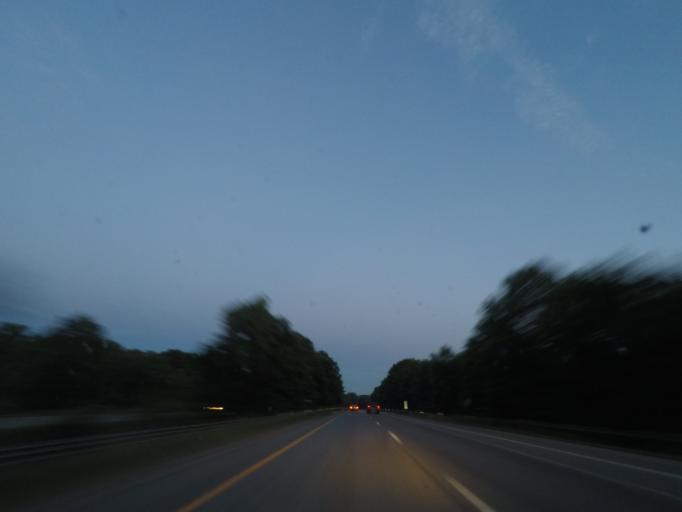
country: US
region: Connecticut
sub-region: Windham County
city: Putnam
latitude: 41.8960
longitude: -71.8979
